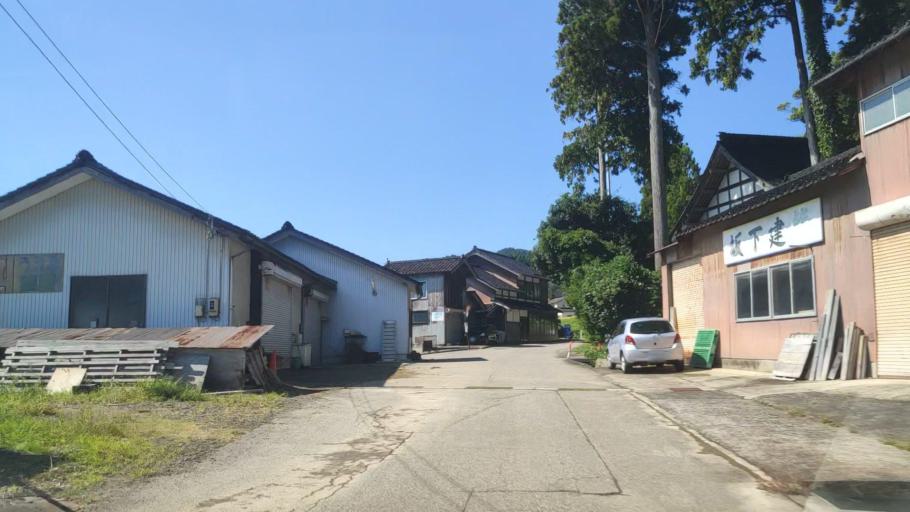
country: JP
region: Ishikawa
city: Nanao
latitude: 37.3714
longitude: 136.8725
